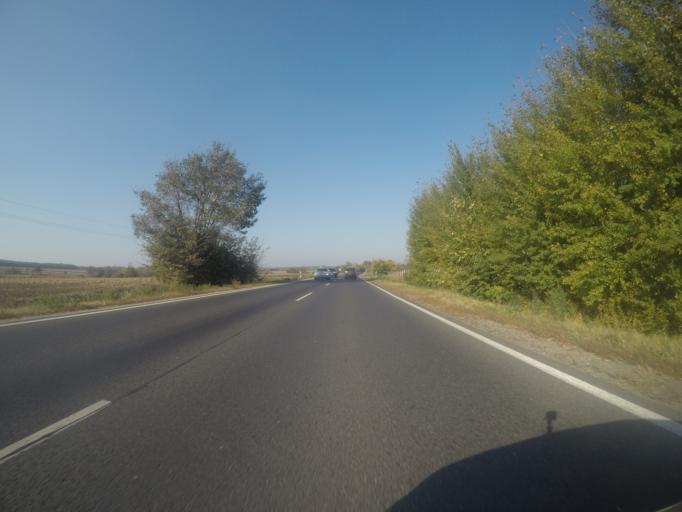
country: HU
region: Tolna
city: Dunafoldvar
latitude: 46.8191
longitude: 18.9065
